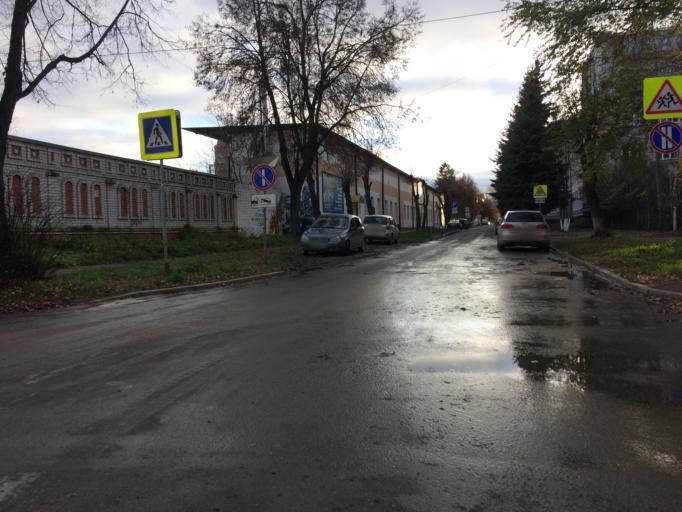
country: RU
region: Mariy-El
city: Yoshkar-Ola
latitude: 56.6421
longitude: 47.8998
